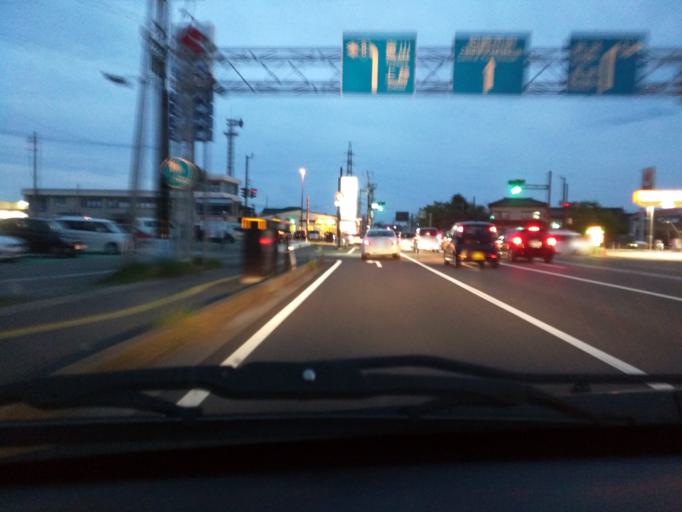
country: JP
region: Niigata
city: Kashiwazaki
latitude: 37.3670
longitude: 138.5757
